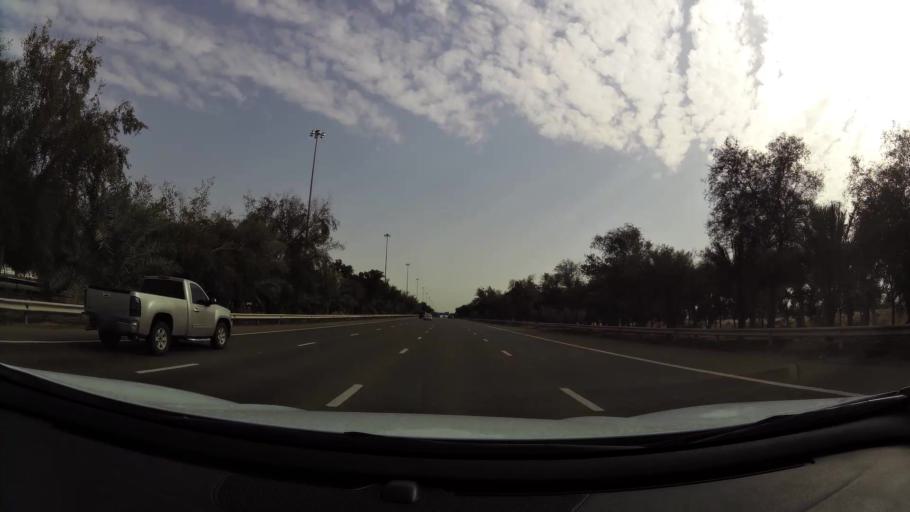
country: AE
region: Abu Dhabi
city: Abu Dhabi
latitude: 24.4801
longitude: 54.6751
